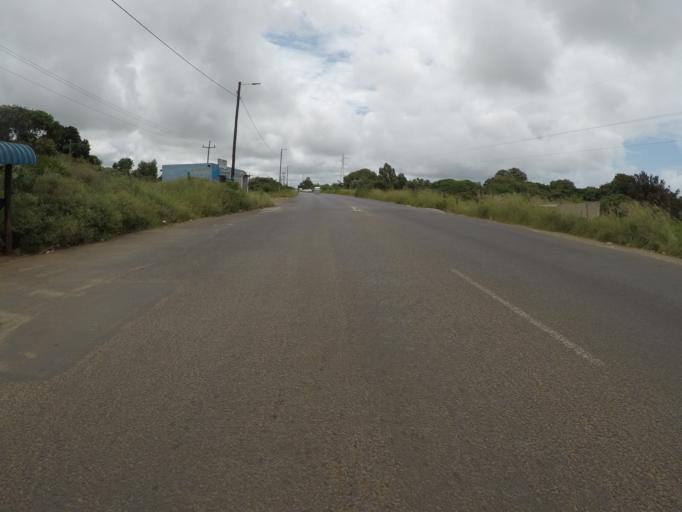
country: ZA
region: KwaZulu-Natal
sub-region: uThungulu District Municipality
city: eSikhawini
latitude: -28.8452
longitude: 31.9322
